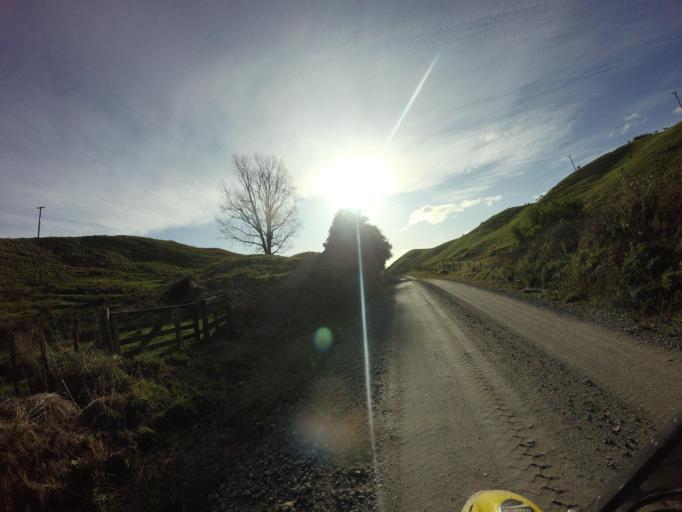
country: NZ
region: Hawke's Bay
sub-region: Wairoa District
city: Wairoa
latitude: -38.7524
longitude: 177.5401
